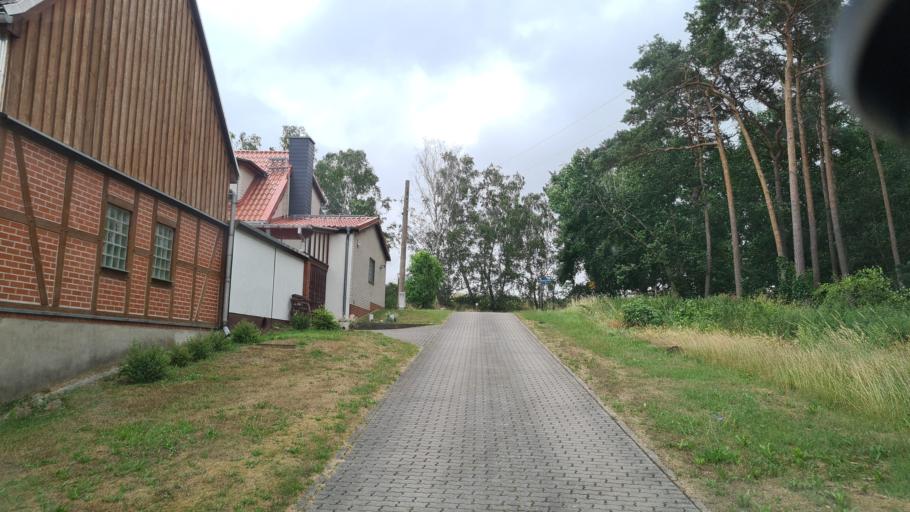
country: DE
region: Brandenburg
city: Juterbog
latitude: 51.9691
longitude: 13.1687
